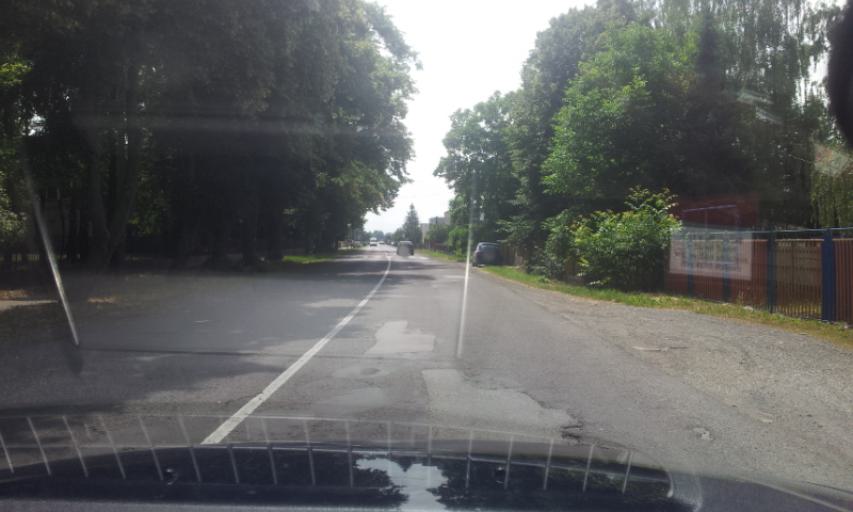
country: SK
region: Kosicky
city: Michalovce
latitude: 48.7436
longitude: 21.9398
